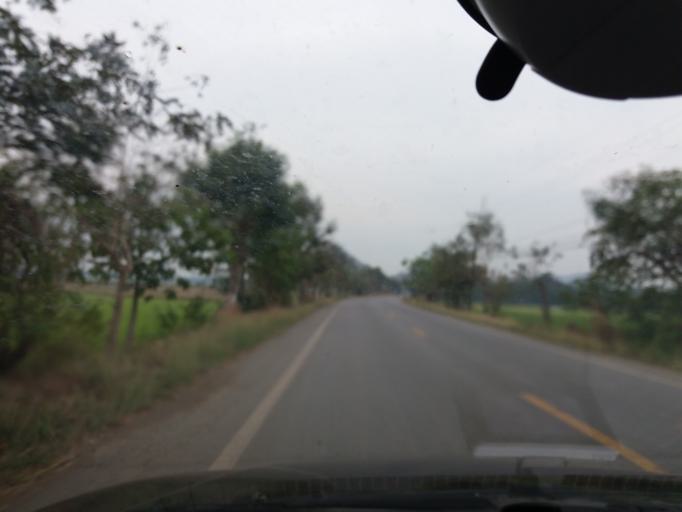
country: TH
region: Suphan Buri
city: Doembang Nangbuat
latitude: 14.8369
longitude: 100.1255
